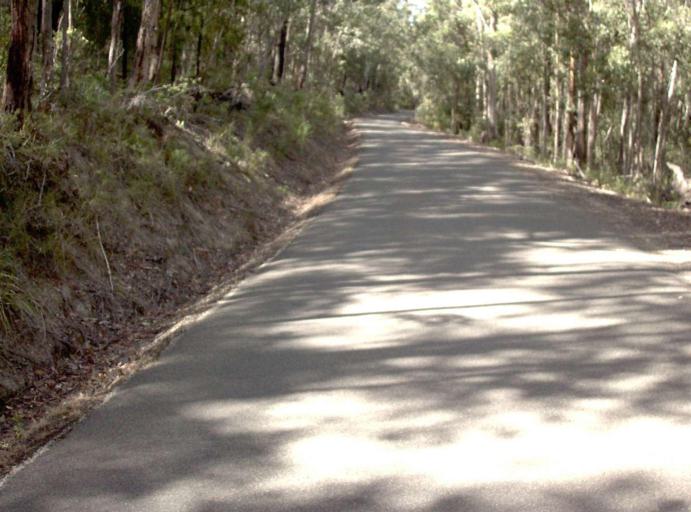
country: AU
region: Victoria
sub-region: East Gippsland
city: Lakes Entrance
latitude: -37.4500
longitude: 148.1263
